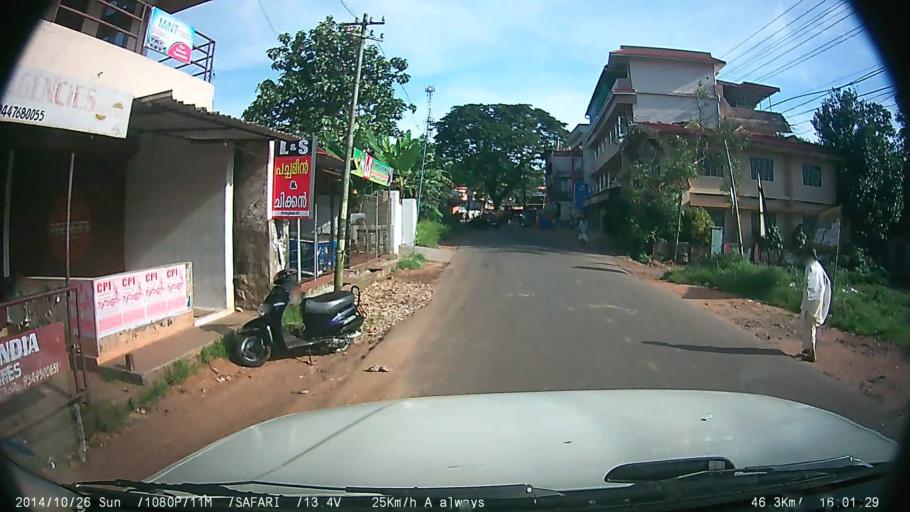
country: IN
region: Kerala
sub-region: Kottayam
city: Changanacheri
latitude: 9.4263
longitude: 76.5612
